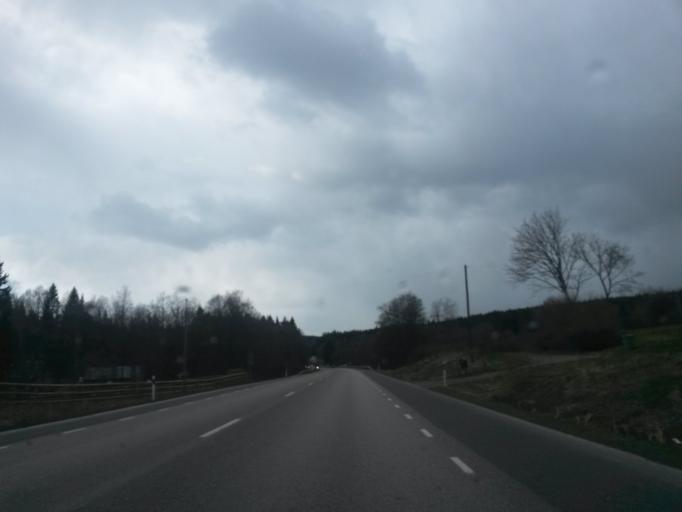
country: SE
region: Vaestra Goetaland
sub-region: Skovde Kommun
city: Skoevde
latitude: 58.3896
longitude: 13.7903
